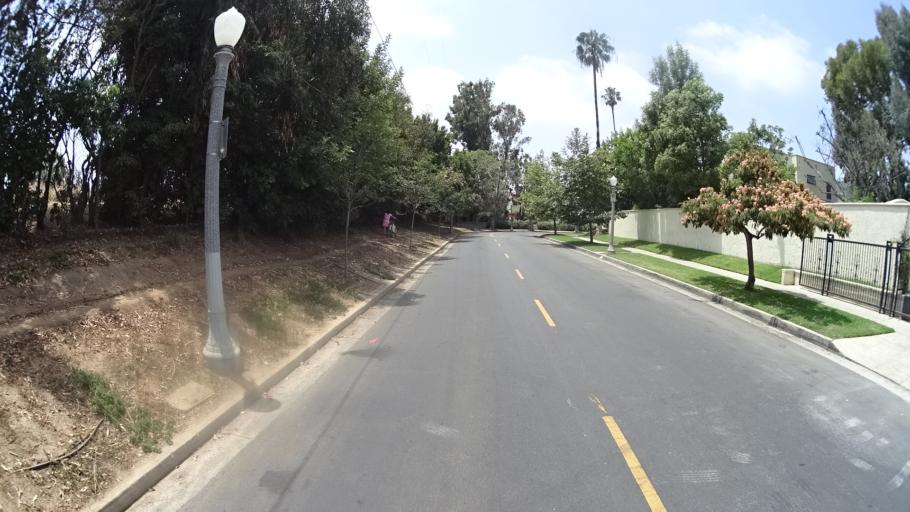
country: US
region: California
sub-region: Los Angeles County
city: Hollywood
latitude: 34.0789
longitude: -118.3301
